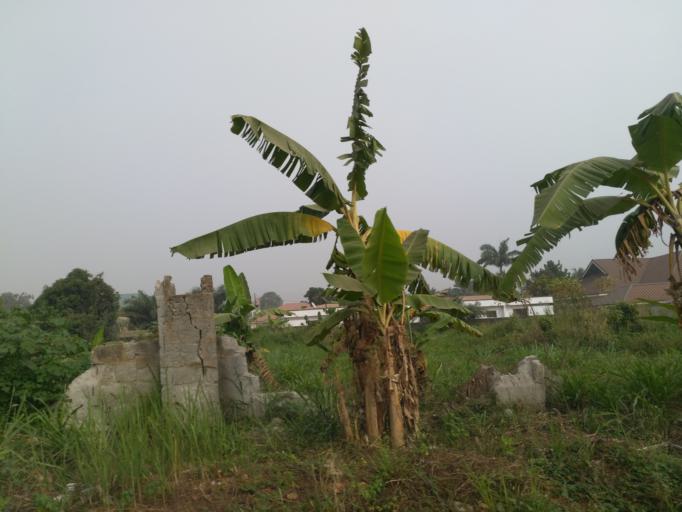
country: GH
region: Ashanti
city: Kumasi
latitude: 6.6564
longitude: -1.6280
